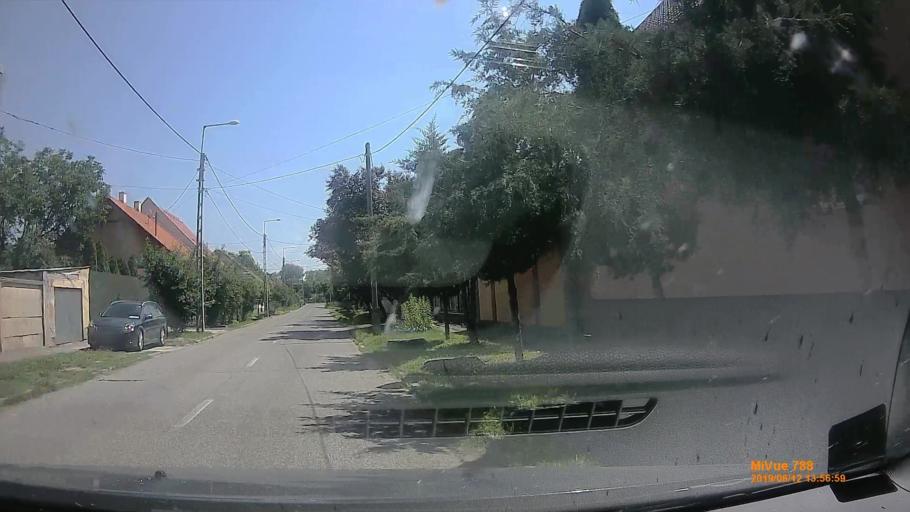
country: HU
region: Csongrad
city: Szeged
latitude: 46.2610
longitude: 20.1811
